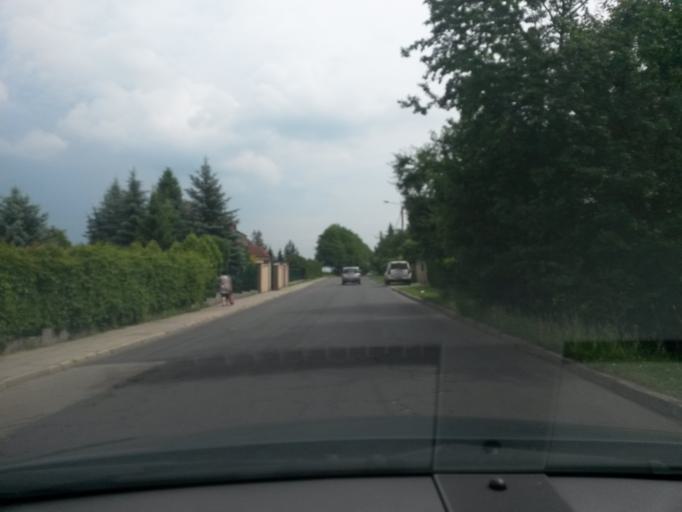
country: PL
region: Silesian Voivodeship
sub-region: Powiat czestochowski
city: Huta Stara B
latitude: 50.7658
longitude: 19.1530
